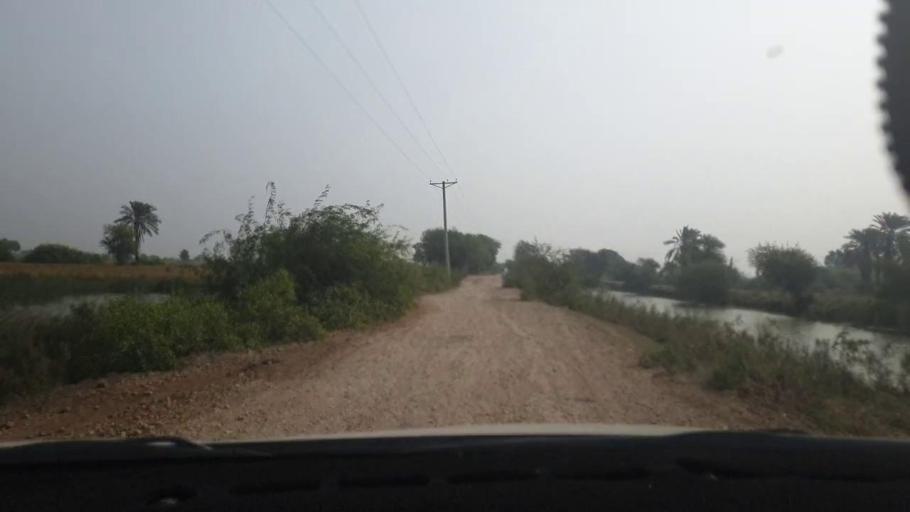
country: PK
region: Sindh
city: Tando Muhammad Khan
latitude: 25.0743
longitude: 68.4991
